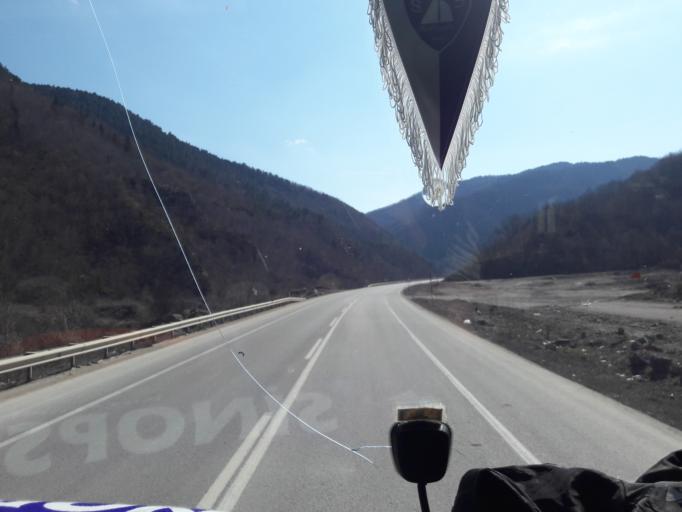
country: TR
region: Sinop
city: Erfelek
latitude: 41.7019
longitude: 34.9151
